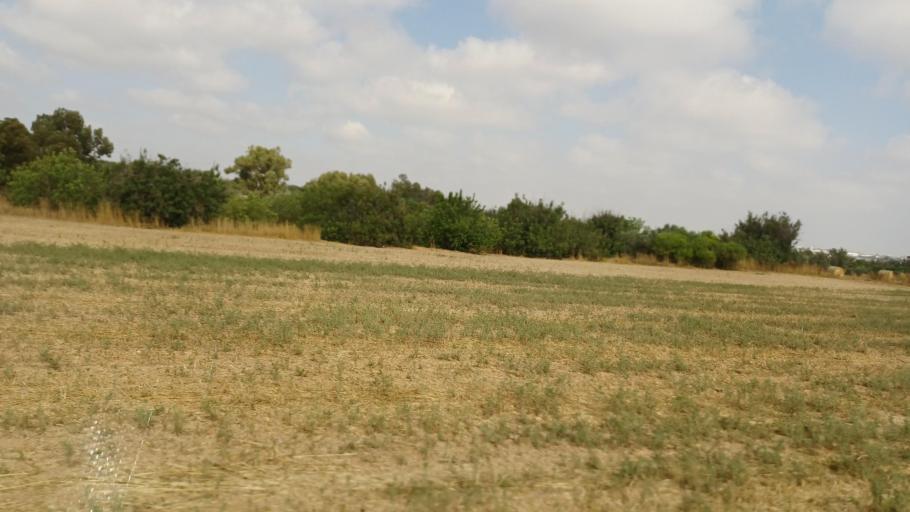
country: CY
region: Ammochostos
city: Ayia Napa
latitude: 35.0126
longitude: 34.0078
